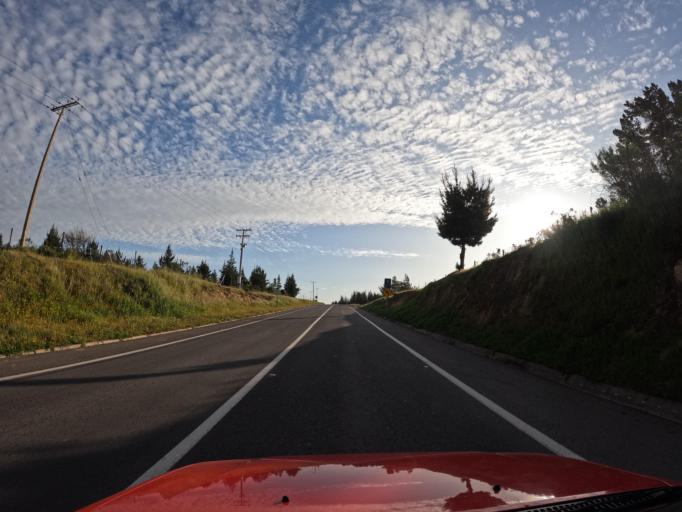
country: CL
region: Valparaiso
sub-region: San Antonio Province
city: San Antonio
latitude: -34.0505
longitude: -71.6218
